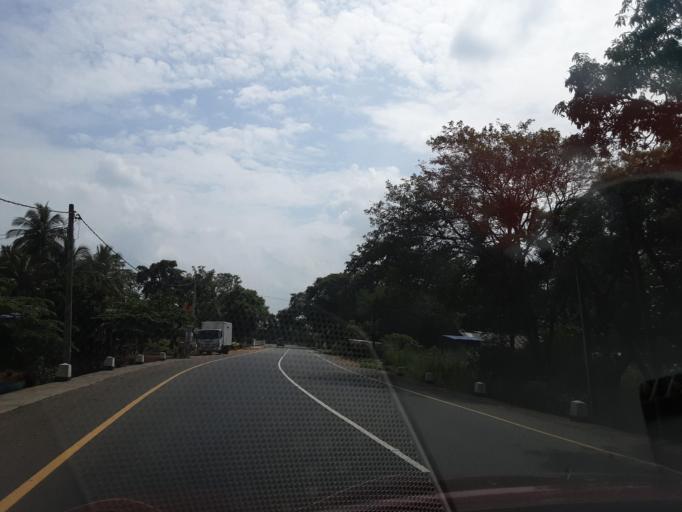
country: LK
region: North Central
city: Anuradhapura
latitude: 8.5119
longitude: 80.5057
